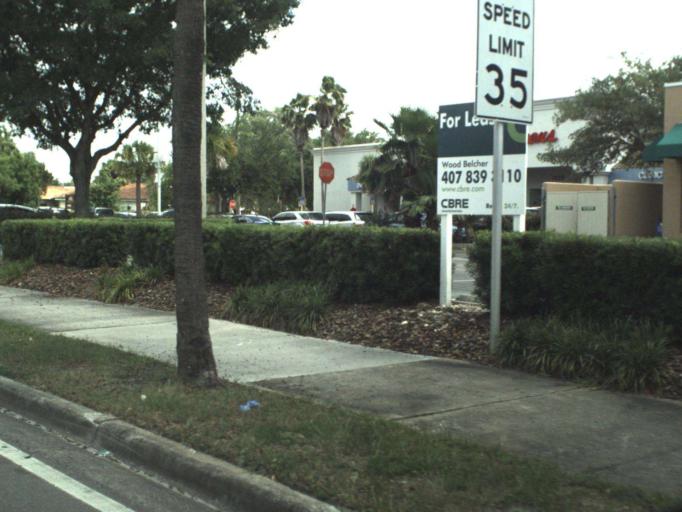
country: US
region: Florida
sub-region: Orange County
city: Winter Park
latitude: 28.6004
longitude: -81.3277
